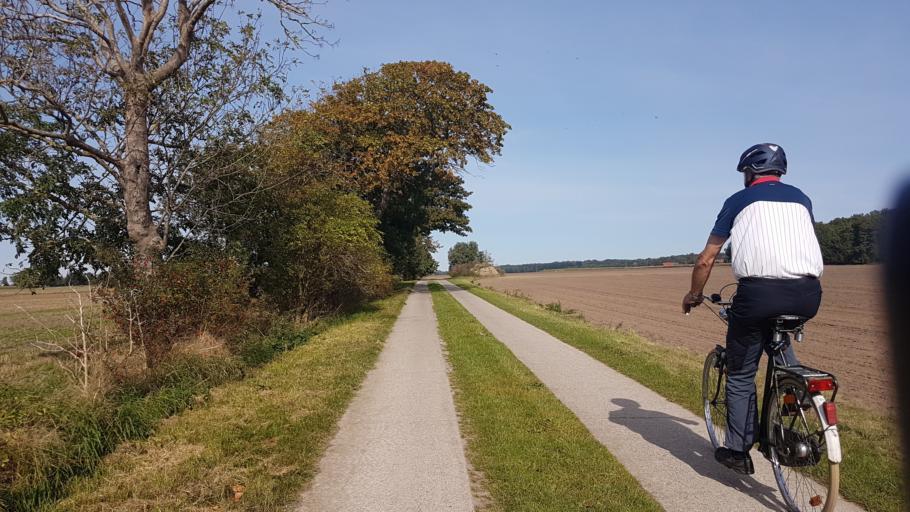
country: DE
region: Mecklenburg-Vorpommern
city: Gingst
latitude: 54.4111
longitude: 13.2574
